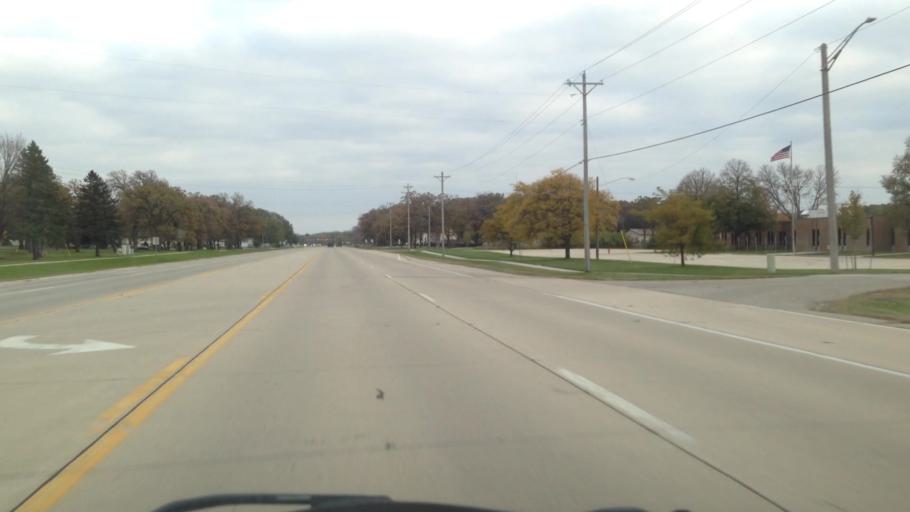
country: US
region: Minnesota
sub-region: Olmsted County
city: Rochester
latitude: 43.9979
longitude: -92.4310
